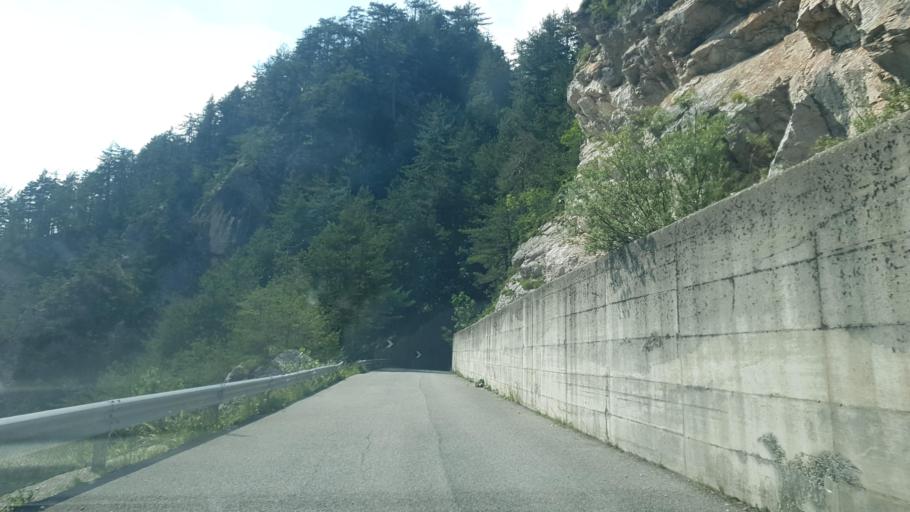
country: IT
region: Friuli Venezia Giulia
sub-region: Provincia di Udine
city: Malborghetto
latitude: 46.4561
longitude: 13.3921
